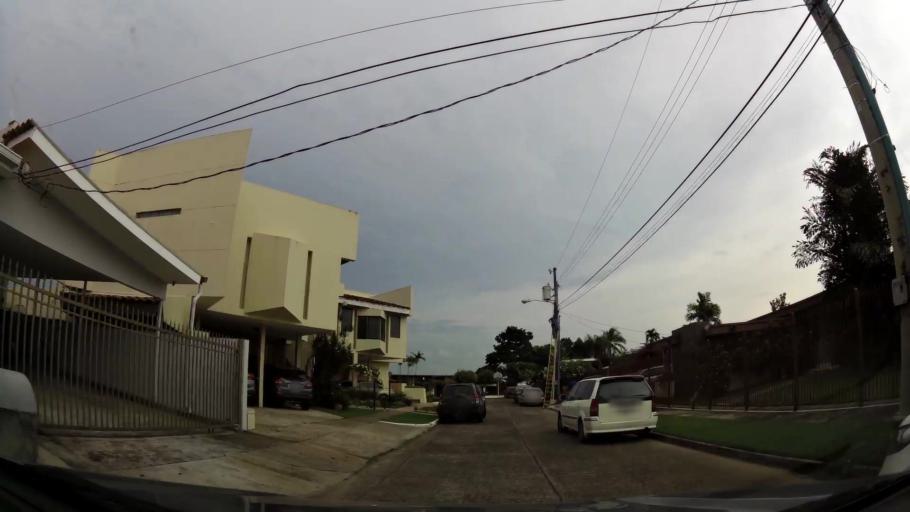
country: PA
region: Panama
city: Panama
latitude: 9.0101
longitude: -79.5301
